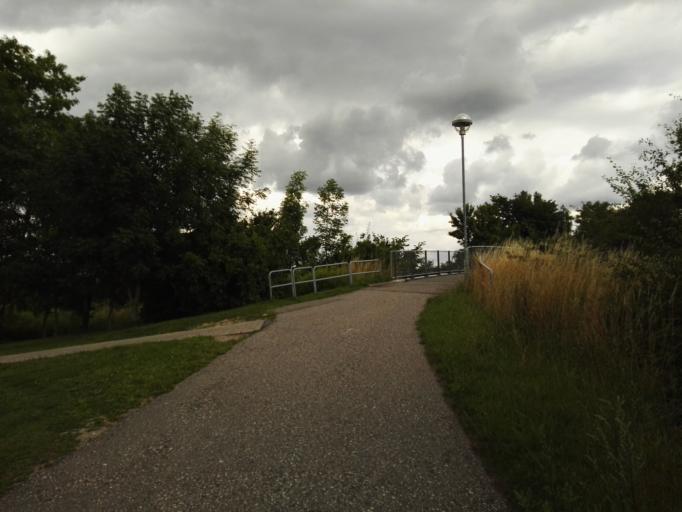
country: DK
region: Capital Region
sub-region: Egedal Kommune
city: Stenlose
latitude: 55.7631
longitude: 12.1910
